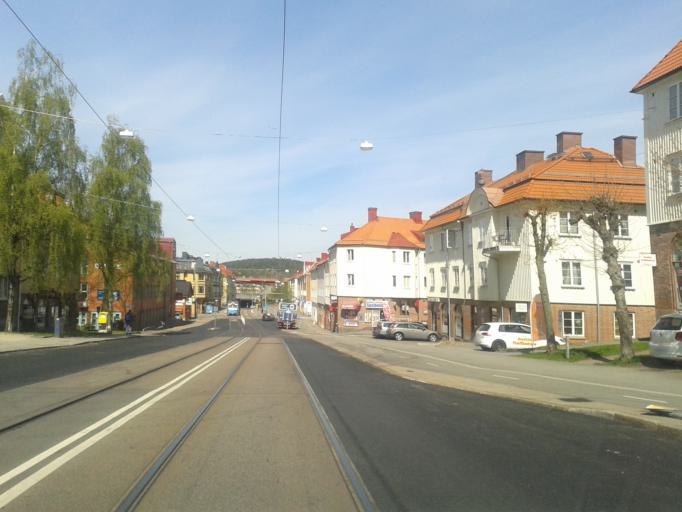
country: SE
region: Vaestra Goetaland
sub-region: Goteborg
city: Goeteborg
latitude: 57.7192
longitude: 12.0055
